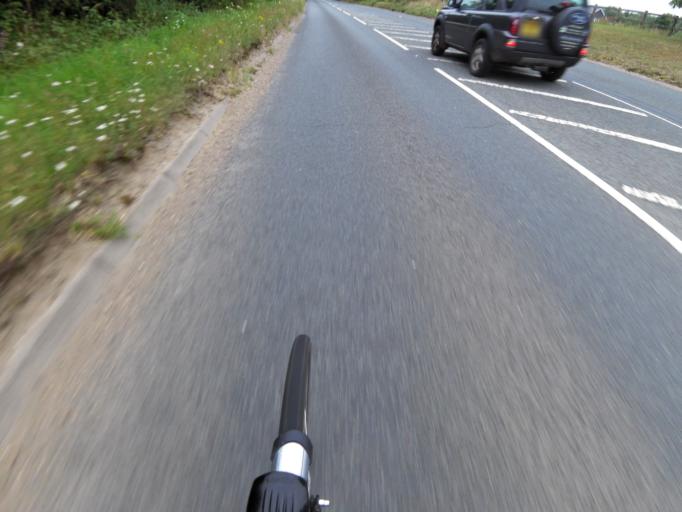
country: GB
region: England
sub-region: Suffolk
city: Bramford
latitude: 52.0910
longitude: 1.0913
